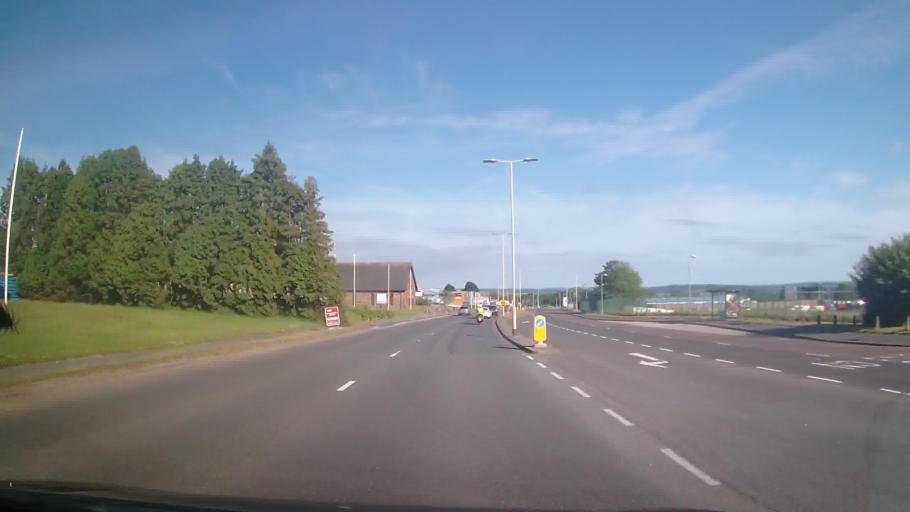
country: GB
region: England
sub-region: Devon
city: Plympton
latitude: 50.4207
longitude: -4.0953
